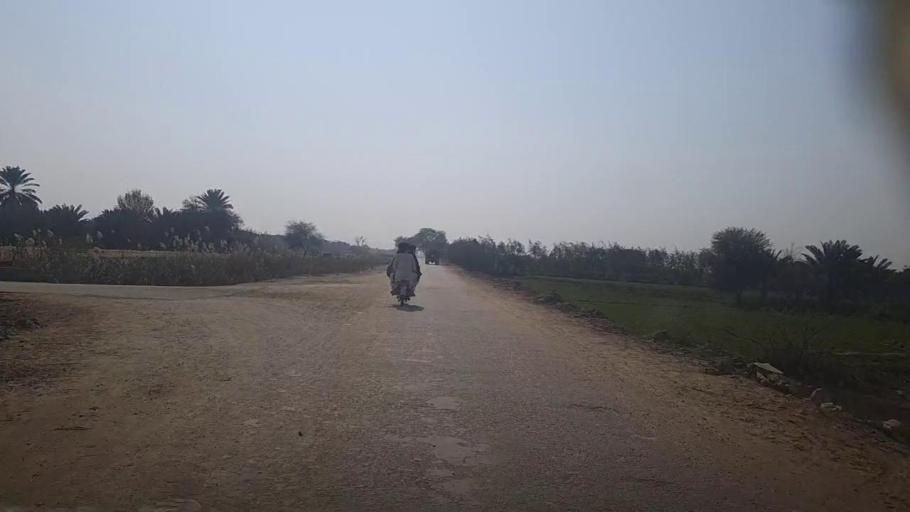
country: PK
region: Sindh
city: Khairpur
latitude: 27.4617
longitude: 68.8165
